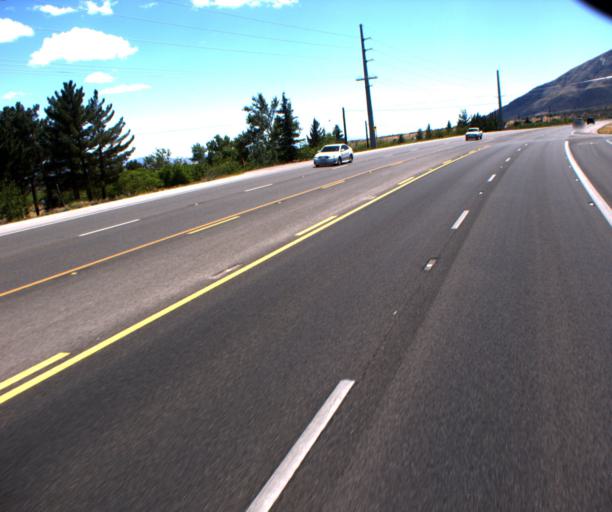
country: US
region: Arizona
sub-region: Cochise County
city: Sierra Vista Southeast
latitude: 31.4297
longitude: -110.2410
